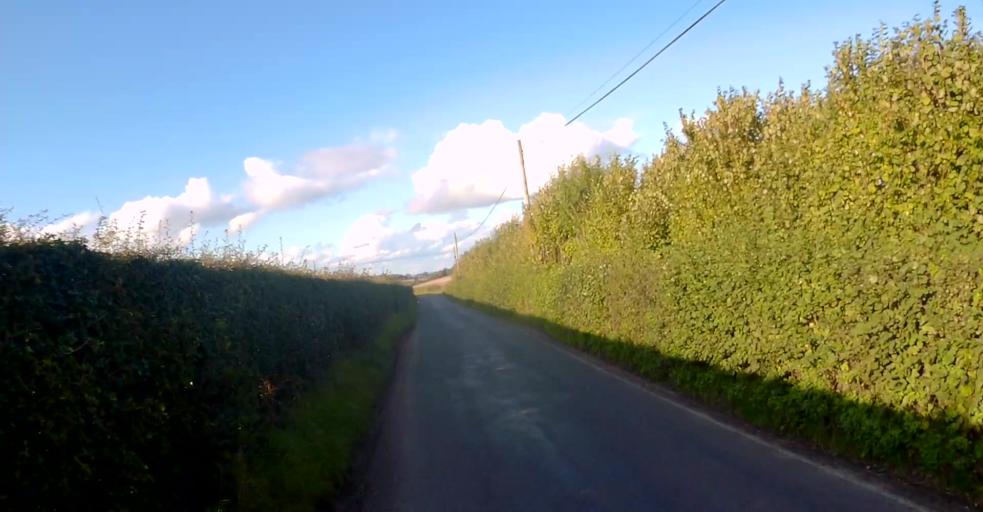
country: GB
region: England
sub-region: Hampshire
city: Long Sutton
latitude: 51.2240
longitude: -0.9229
